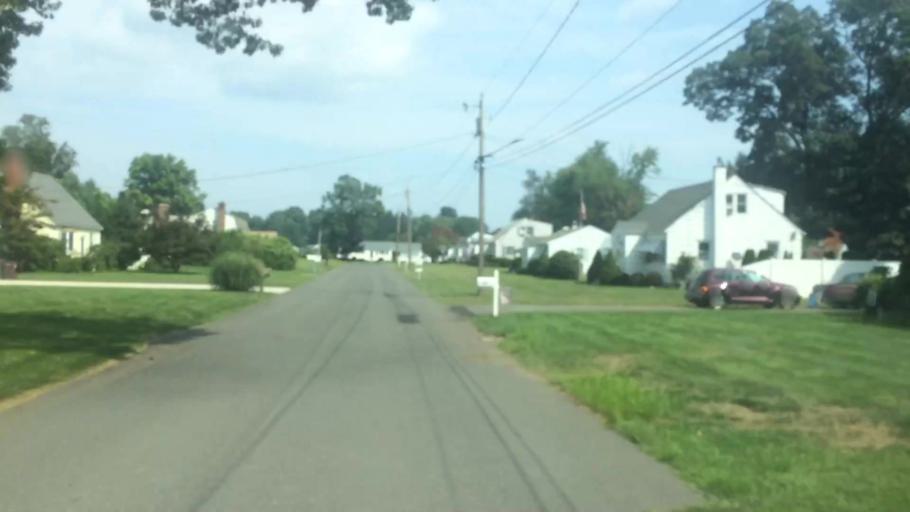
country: US
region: Massachusetts
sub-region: Hampden County
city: Westfield
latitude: 42.1415
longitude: -72.7561
